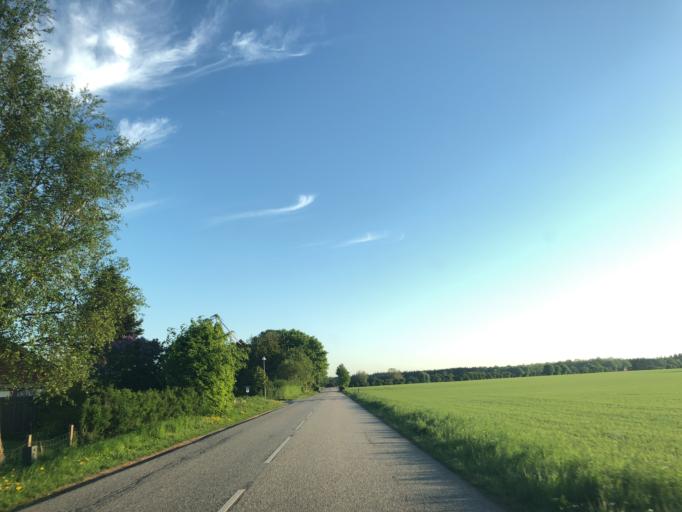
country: DK
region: Zealand
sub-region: Koge Kommune
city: Borup
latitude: 55.4451
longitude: 11.9510
